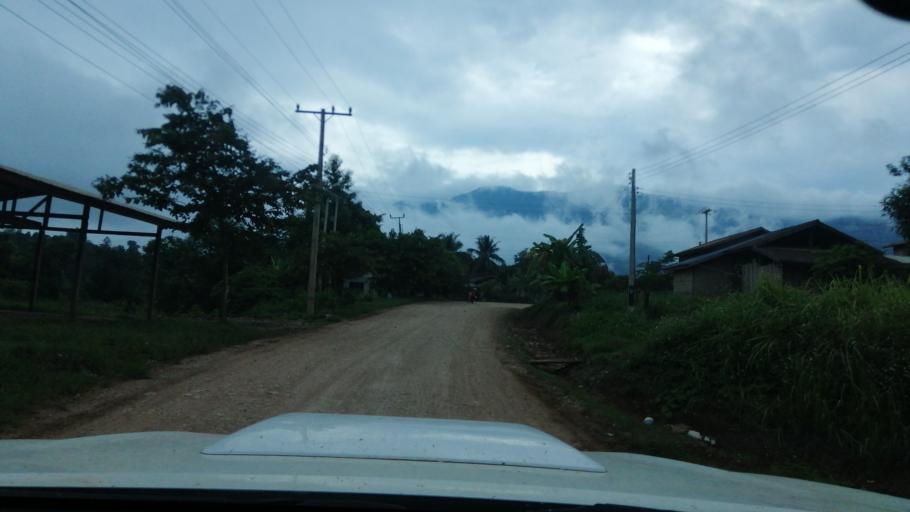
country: LA
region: Xiagnabouli
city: Sainyabuli
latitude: 19.2095
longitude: 101.7127
